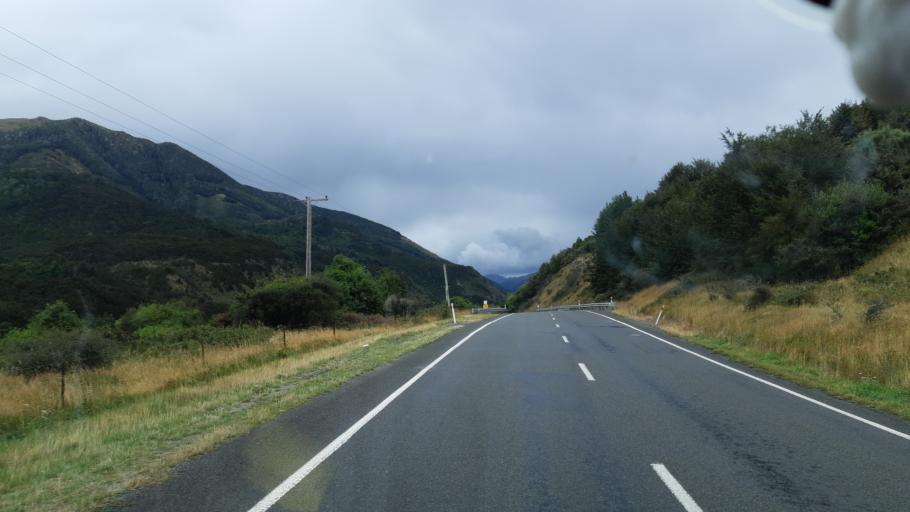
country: NZ
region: Canterbury
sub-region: Hurunui District
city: Amberley
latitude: -42.5716
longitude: 172.3670
